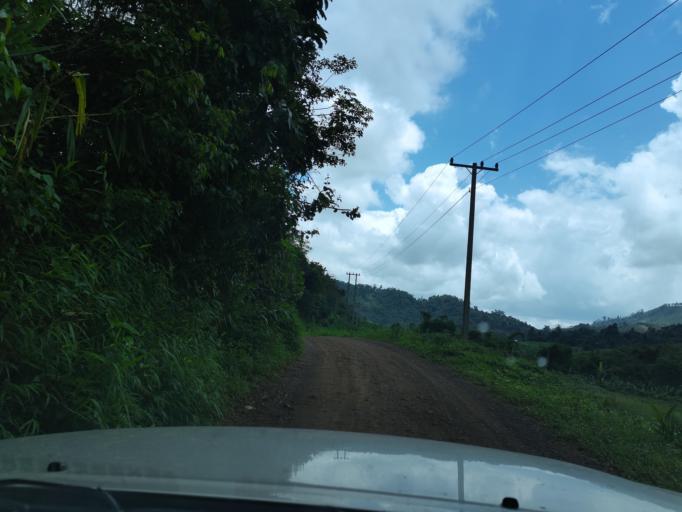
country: LA
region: Loungnamtha
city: Muang Long
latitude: 20.7540
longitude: 101.0179
